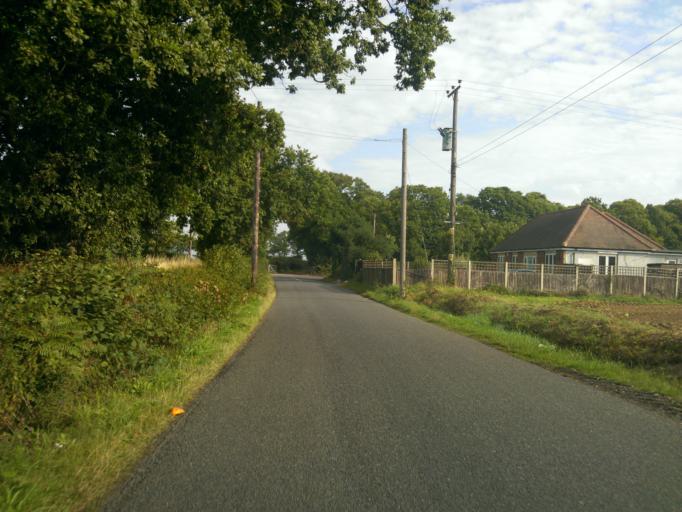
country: GB
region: England
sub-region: Essex
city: Little Clacton
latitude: 51.8395
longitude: 1.1045
